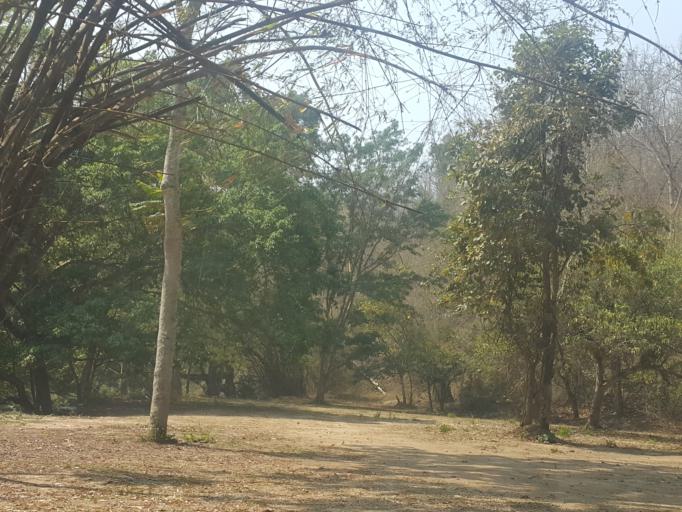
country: TH
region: Chiang Mai
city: Hang Dong
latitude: 18.7177
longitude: 98.8228
